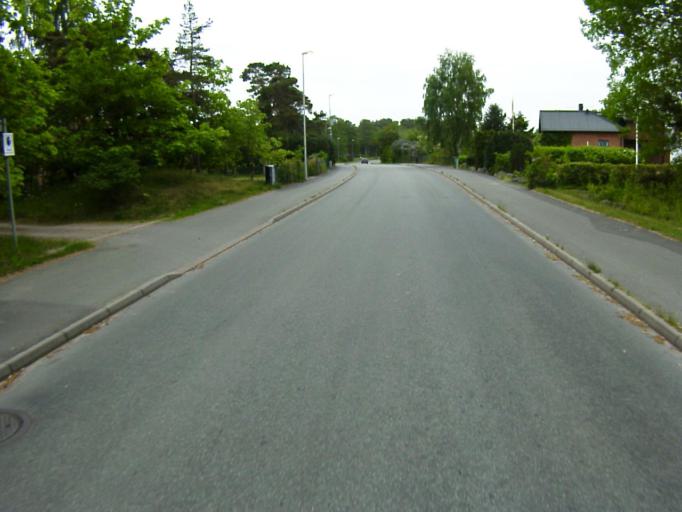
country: SE
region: Skane
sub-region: Kristianstads Kommun
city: Ahus
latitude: 55.9159
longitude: 14.2877
